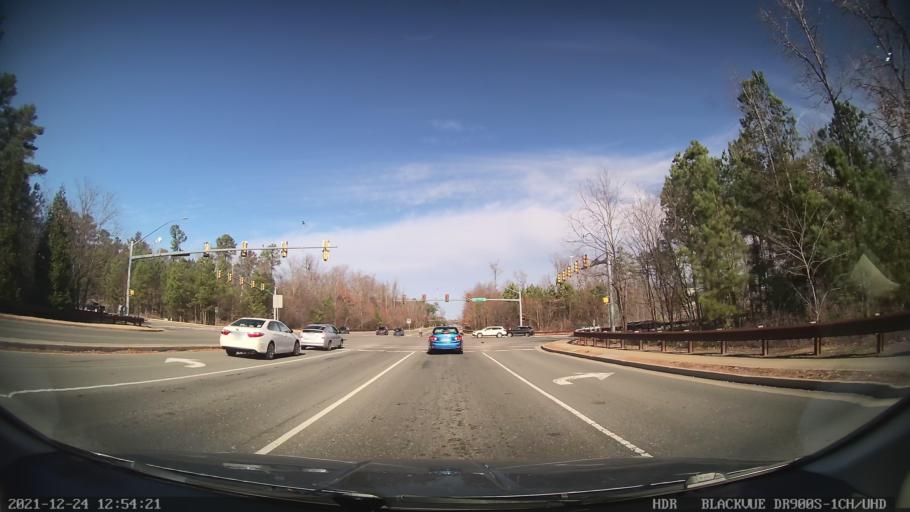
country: US
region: Virginia
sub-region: Henrico County
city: Short Pump
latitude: 37.6443
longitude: -77.6104
